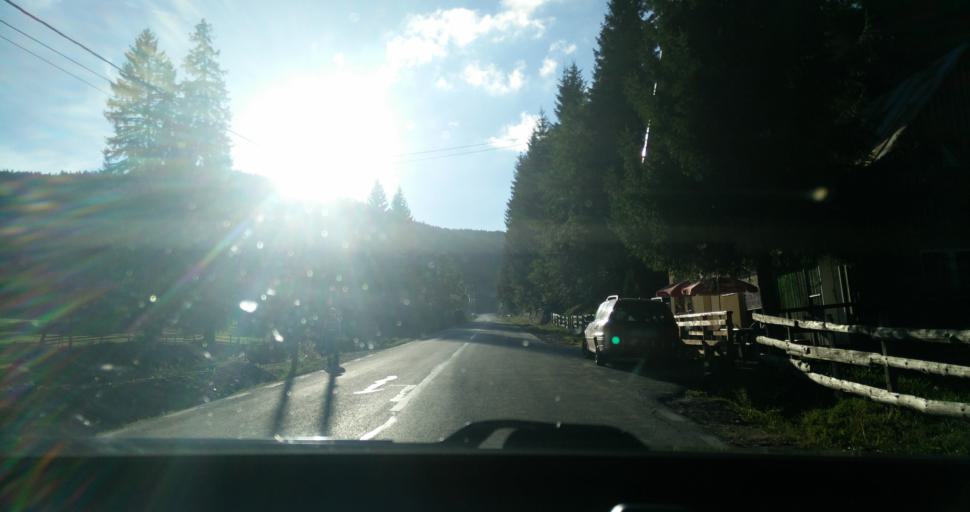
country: RO
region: Alba
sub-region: Comuna Arieseni
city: Arieseni
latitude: 46.5060
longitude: 22.7016
